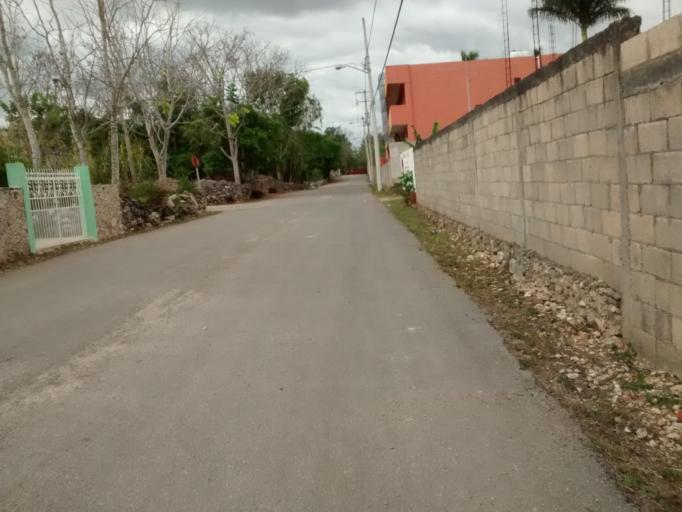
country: MX
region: Yucatan
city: Valladolid
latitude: 20.6816
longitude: -88.1839
